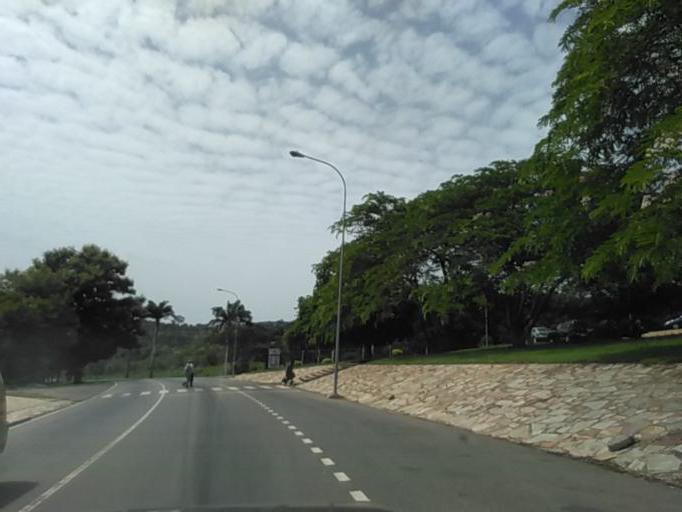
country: GH
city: Akropong
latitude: 6.2645
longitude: 0.0587
